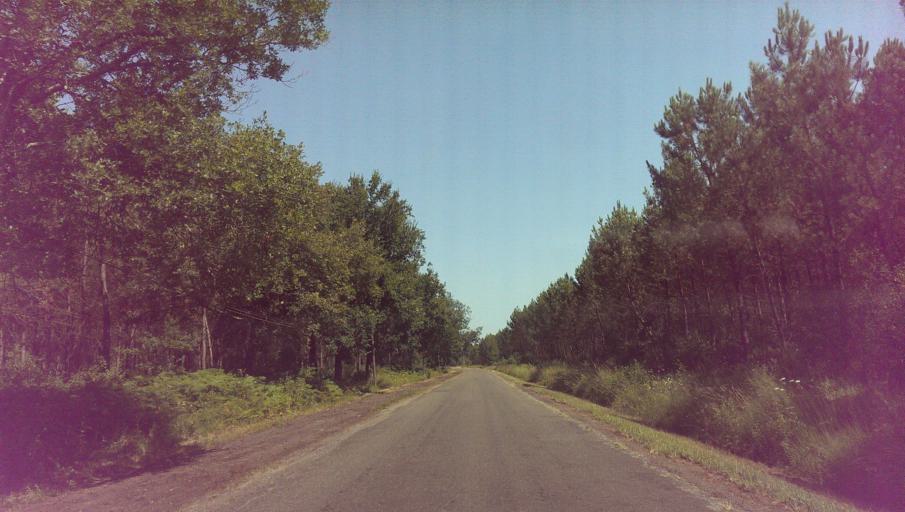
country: FR
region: Midi-Pyrenees
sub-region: Departement du Gers
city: Cazaubon
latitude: 44.0745
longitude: -0.1558
